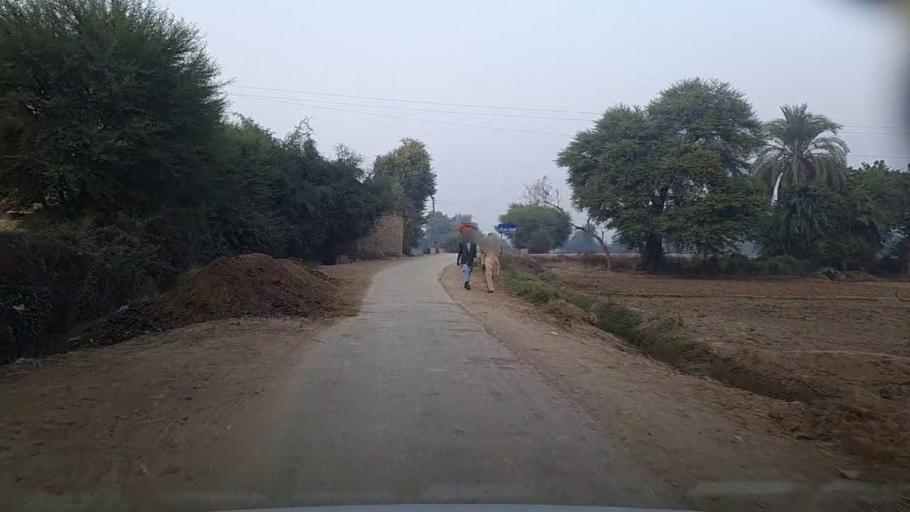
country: PK
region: Sindh
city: Bozdar
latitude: 27.0619
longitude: 68.5955
